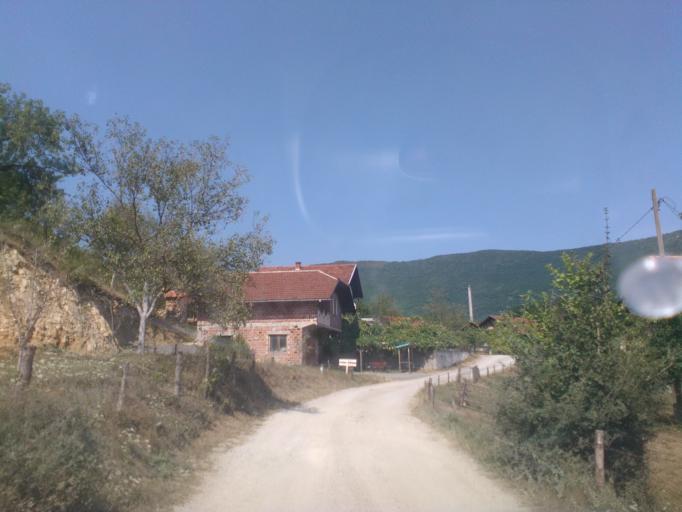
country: BA
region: Federation of Bosnia and Herzegovina
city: Orasac
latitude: 44.6227
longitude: 16.0649
